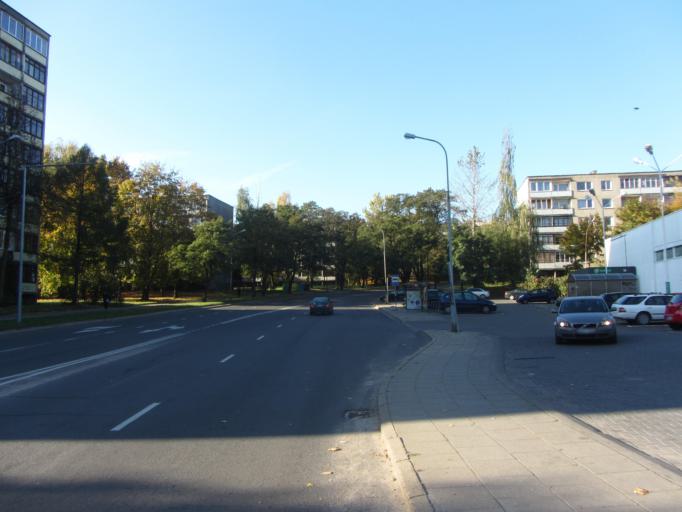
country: LT
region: Vilnius County
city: Lazdynai
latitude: 54.6741
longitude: 25.2013
